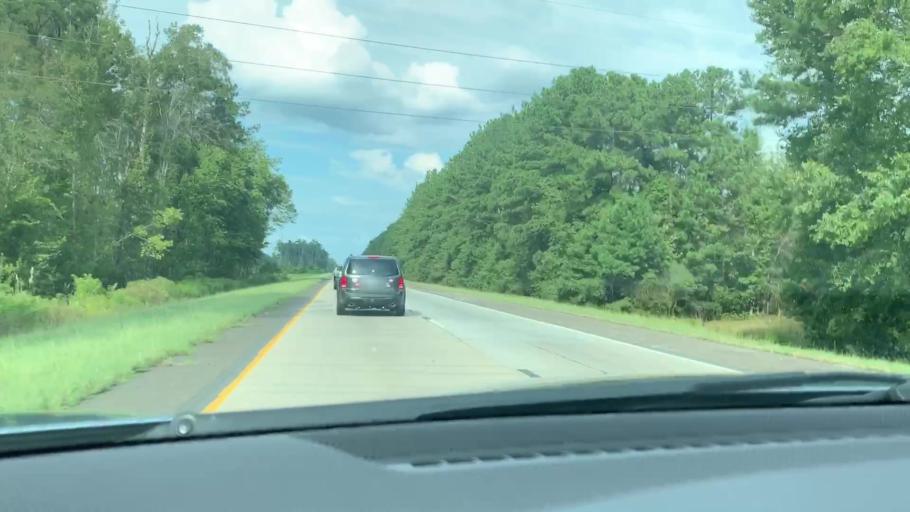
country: US
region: South Carolina
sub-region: Colleton County
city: Walterboro
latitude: 32.8493
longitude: -80.7343
